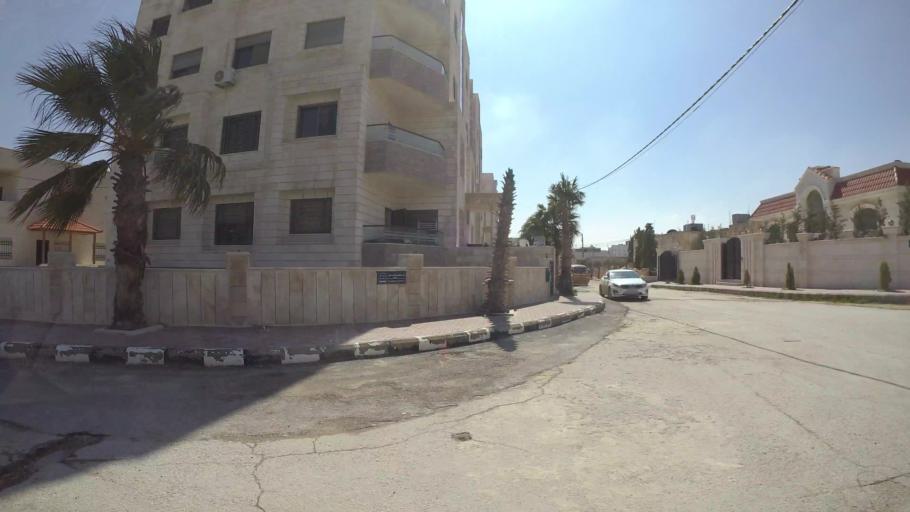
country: JO
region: Amman
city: Al Bunayyat ash Shamaliyah
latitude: 31.9009
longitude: 35.8971
